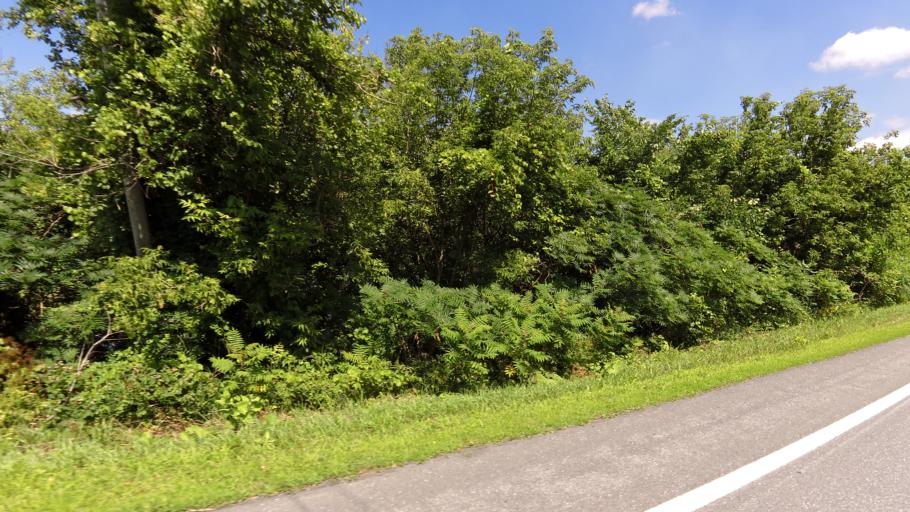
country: CA
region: Quebec
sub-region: Monteregie
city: Richelieu
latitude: 45.4106
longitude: -73.2433
